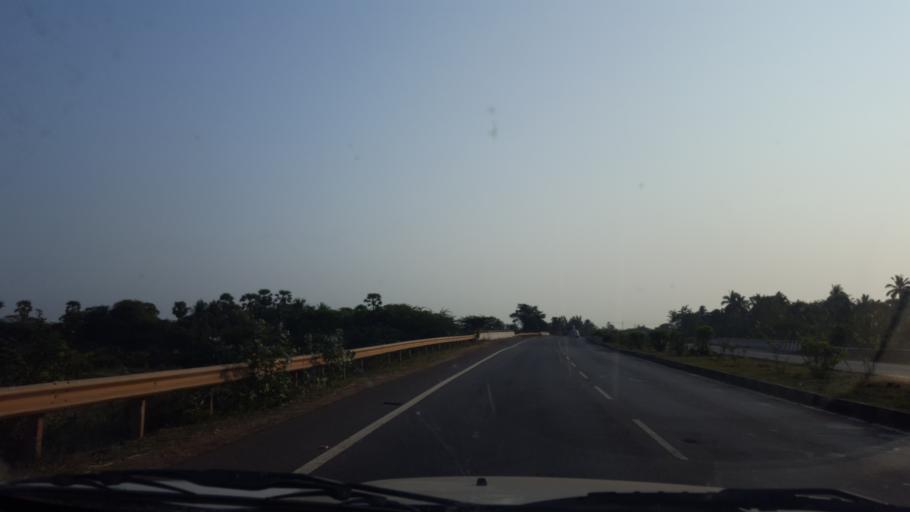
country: IN
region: Andhra Pradesh
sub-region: East Godavari
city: Tuni
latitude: 17.2794
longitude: 82.4165
